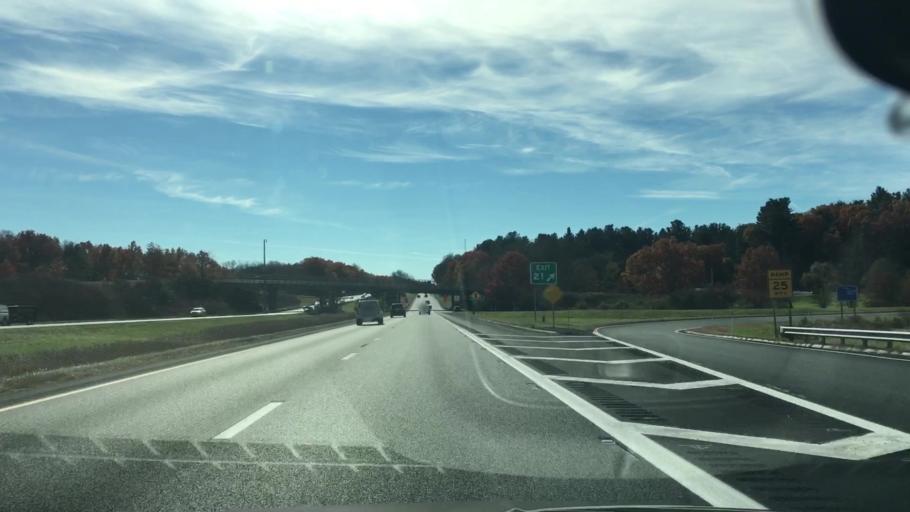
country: US
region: Massachusetts
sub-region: Hampshire County
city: Northampton
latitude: 42.3632
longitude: -72.6361
